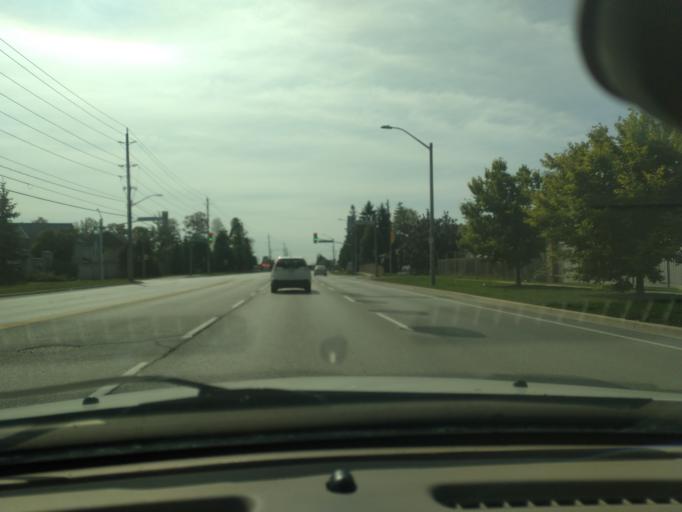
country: CA
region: Ontario
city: Innisfil
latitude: 44.3404
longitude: -79.7008
